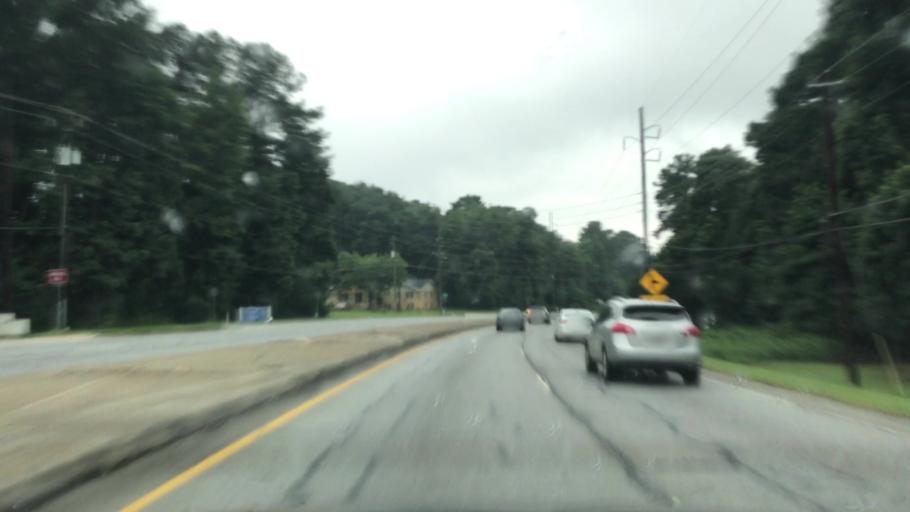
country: US
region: Georgia
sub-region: Gwinnett County
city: Lilburn
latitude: 33.9147
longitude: -84.1361
